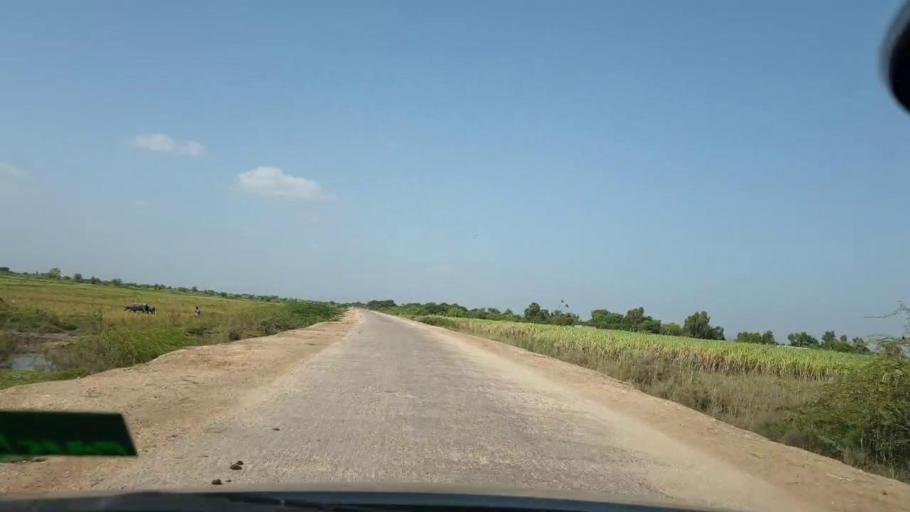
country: PK
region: Sindh
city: Tando Bago
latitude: 24.6880
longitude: 69.1882
